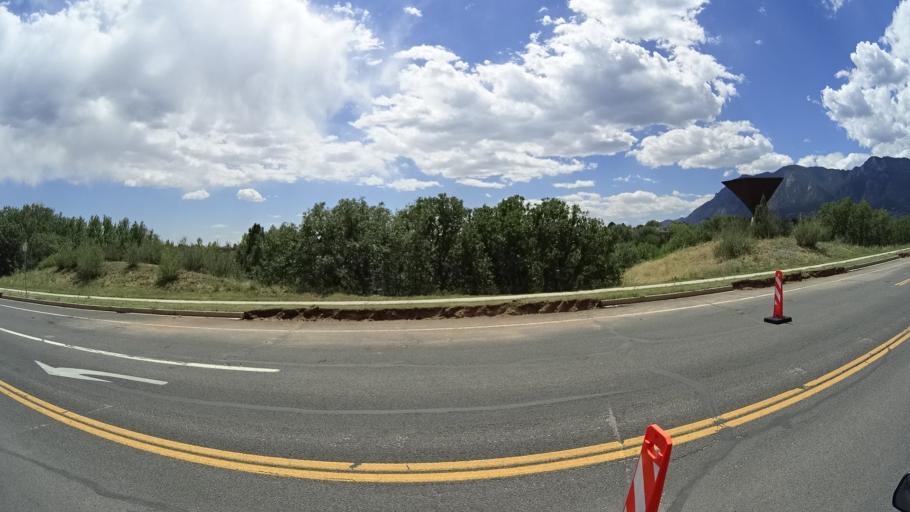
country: US
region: Colorado
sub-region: El Paso County
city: Stratmoor
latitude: 38.7870
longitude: -104.8074
